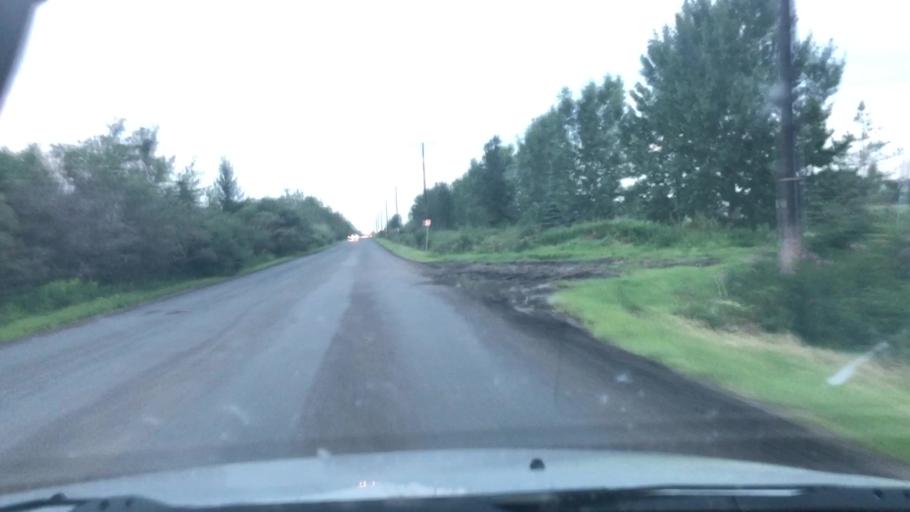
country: CA
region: Alberta
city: Devon
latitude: 53.4913
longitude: -113.6889
